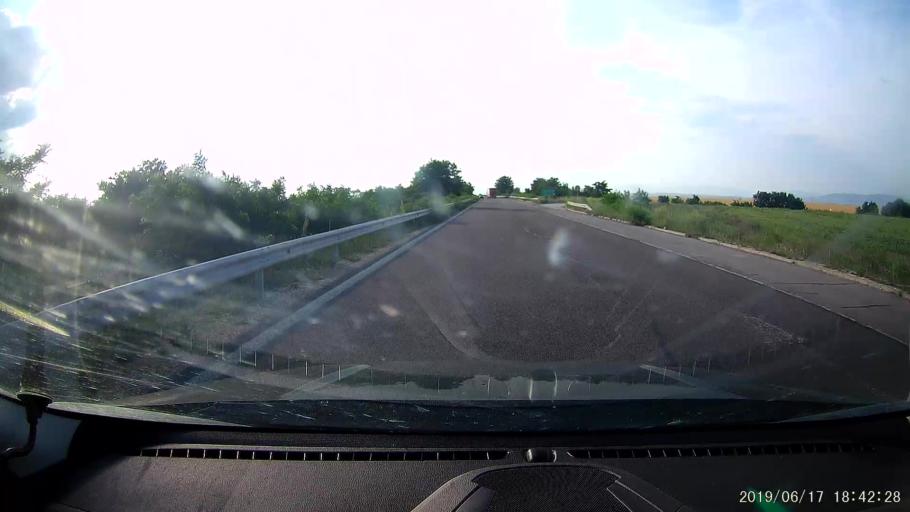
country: BG
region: Stara Zagora
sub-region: Obshtina Chirpan
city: Chirpan
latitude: 42.1917
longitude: 25.2367
